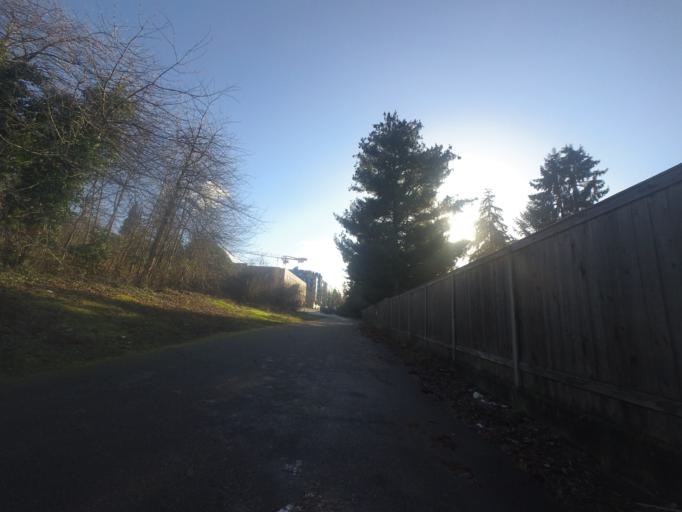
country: US
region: Washington
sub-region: Pierce County
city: University Place
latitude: 47.2279
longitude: -122.5382
